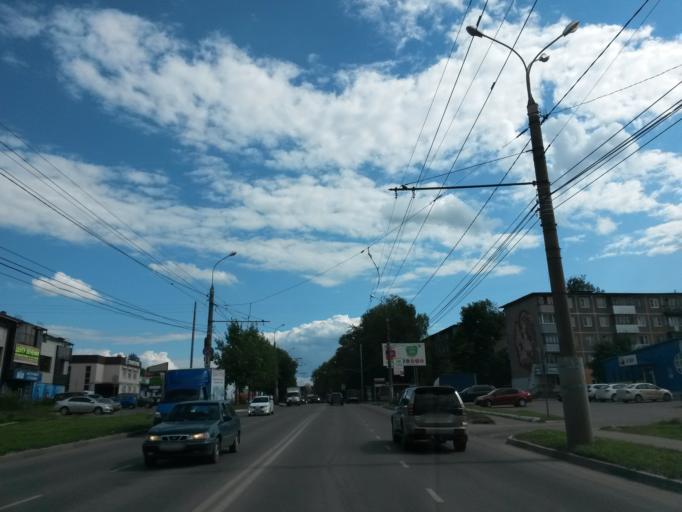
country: RU
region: Ivanovo
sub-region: Gorod Ivanovo
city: Ivanovo
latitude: 56.9753
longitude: 41.0073
